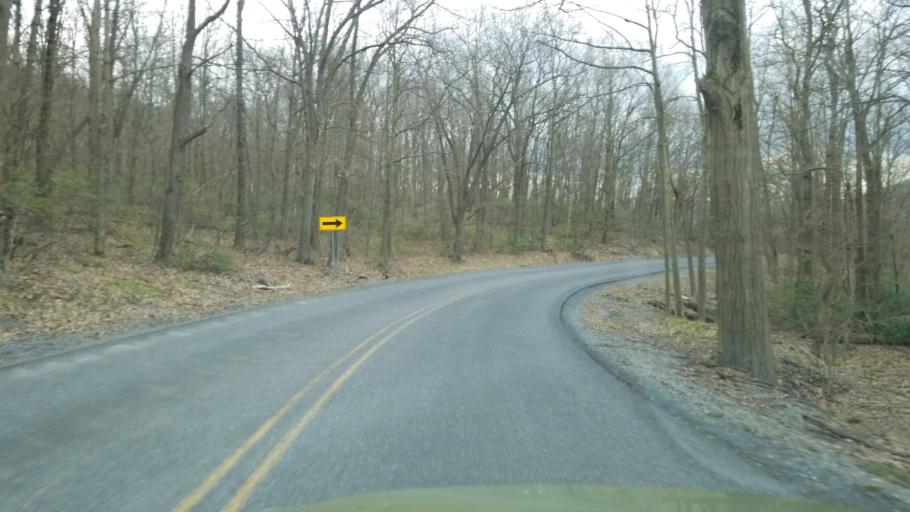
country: US
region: Pennsylvania
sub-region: Blair County
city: Tipton
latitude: 40.7084
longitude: -78.3419
